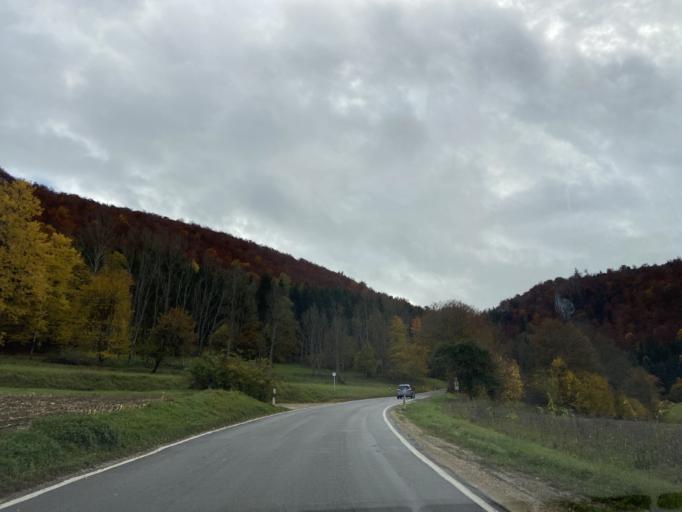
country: DE
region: Baden-Wuerttemberg
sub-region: Tuebingen Region
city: Schwenningen
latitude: 48.0784
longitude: 9.0347
